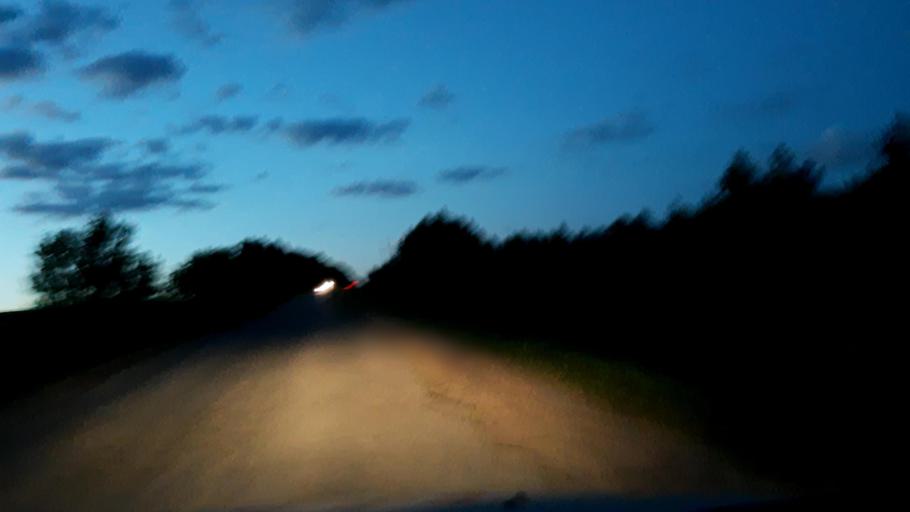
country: RU
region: Nizjnij Novgorod
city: Pamyat' Parizhskoy Kommuny
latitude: 56.0497
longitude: 44.4389
